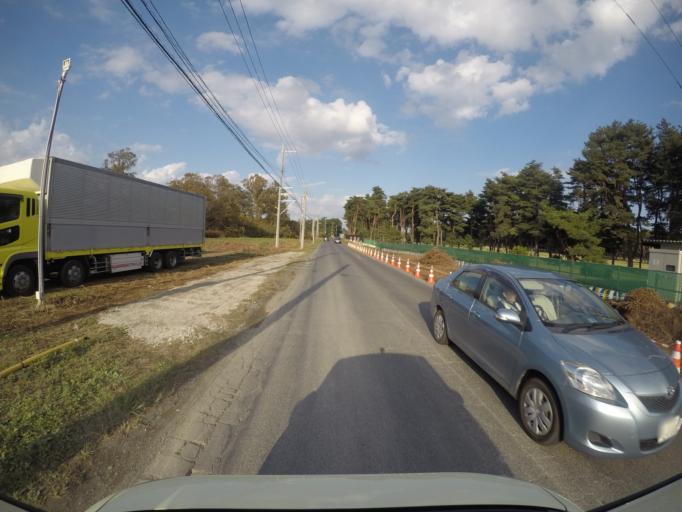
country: JP
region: Ibaraki
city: Mitsukaido
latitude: 36.0044
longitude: 140.0524
